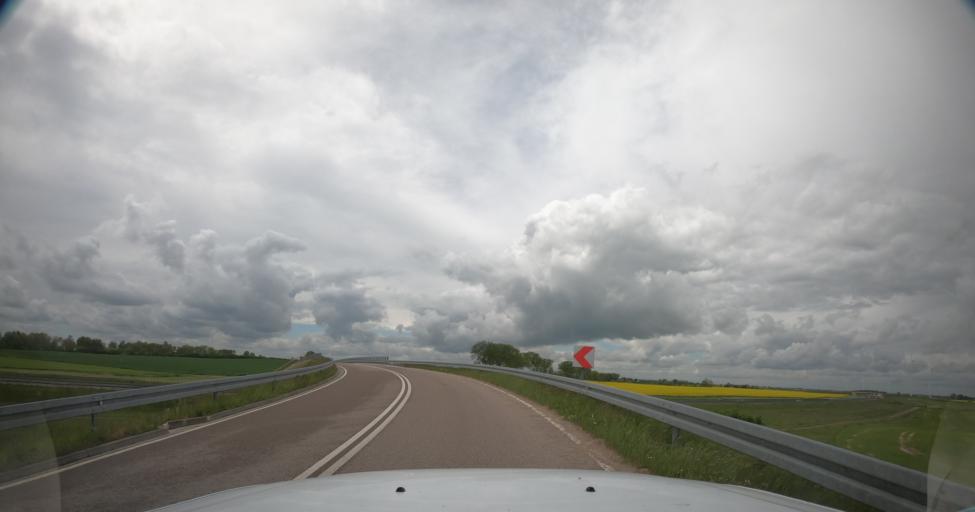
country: PL
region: West Pomeranian Voivodeship
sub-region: Powiat pyrzycki
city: Kozielice
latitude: 53.0805
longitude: 14.8553
